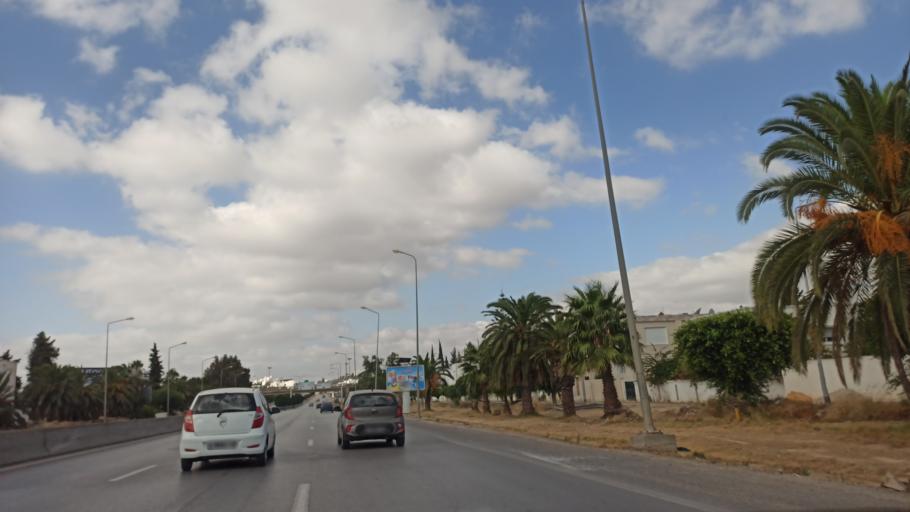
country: TN
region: Ariana
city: Ariana
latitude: 36.8432
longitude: 10.1743
